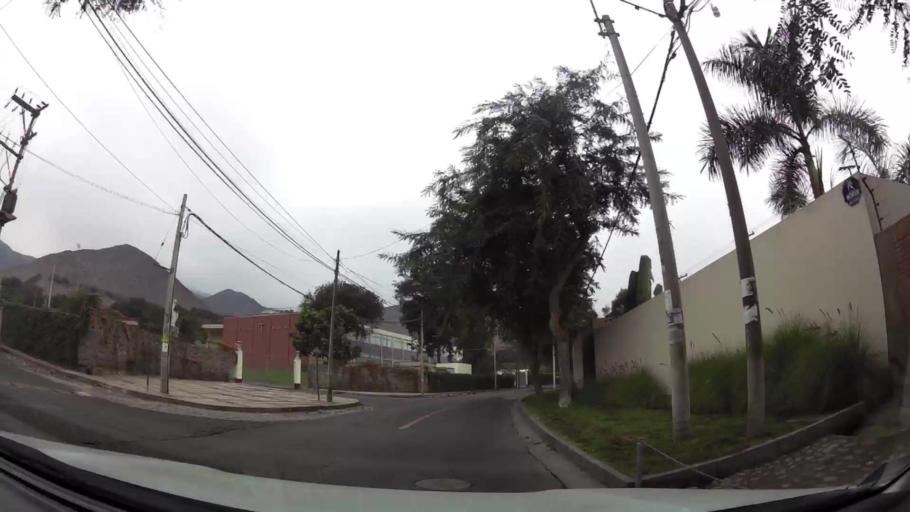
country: PE
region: Lima
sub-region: Lima
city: La Molina
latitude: -12.0710
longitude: -76.9116
